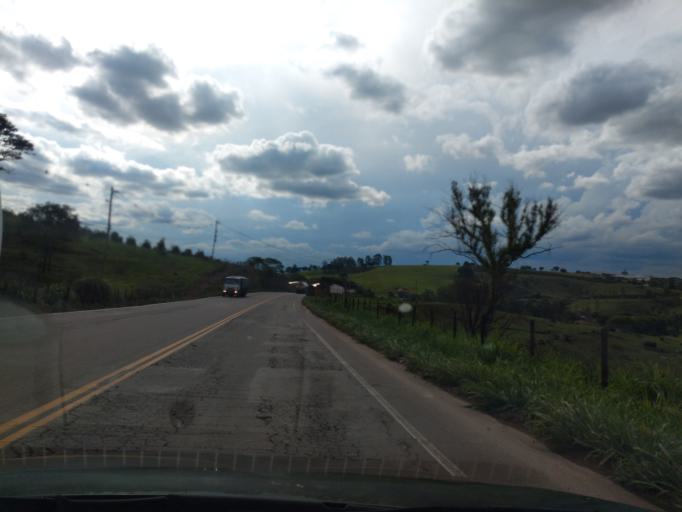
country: BR
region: Minas Gerais
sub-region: Varginha
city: Varginha
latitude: -21.6143
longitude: -45.4227
